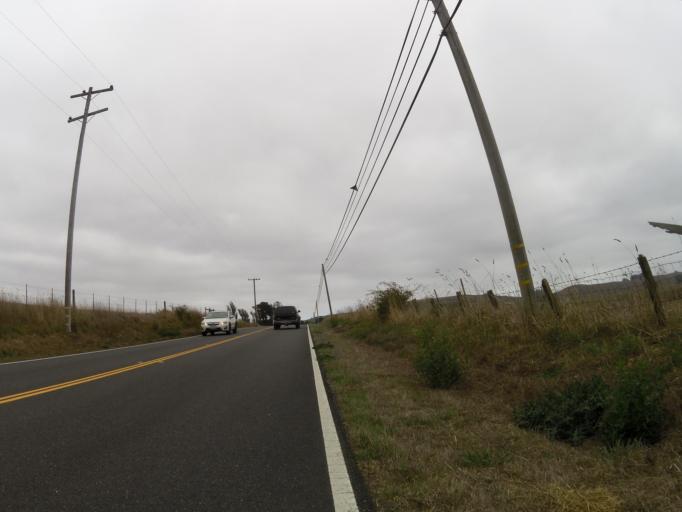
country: US
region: California
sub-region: Sonoma County
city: Occidental
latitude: 38.3185
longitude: -122.9025
